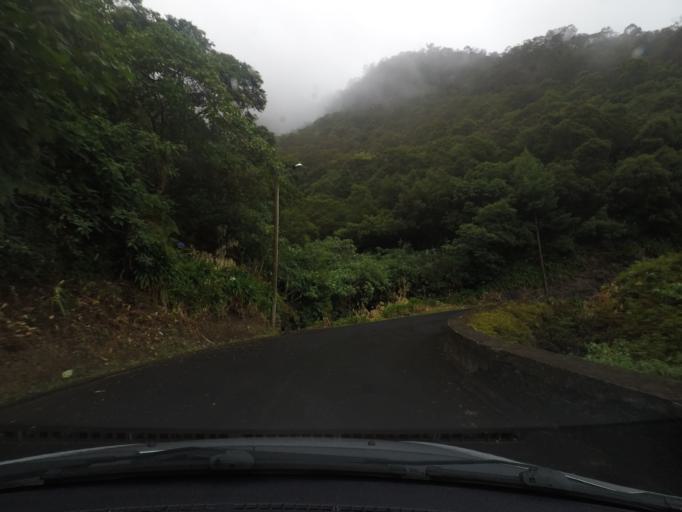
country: PT
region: Madeira
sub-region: Santana
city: Santana
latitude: 32.7848
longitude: -16.8610
